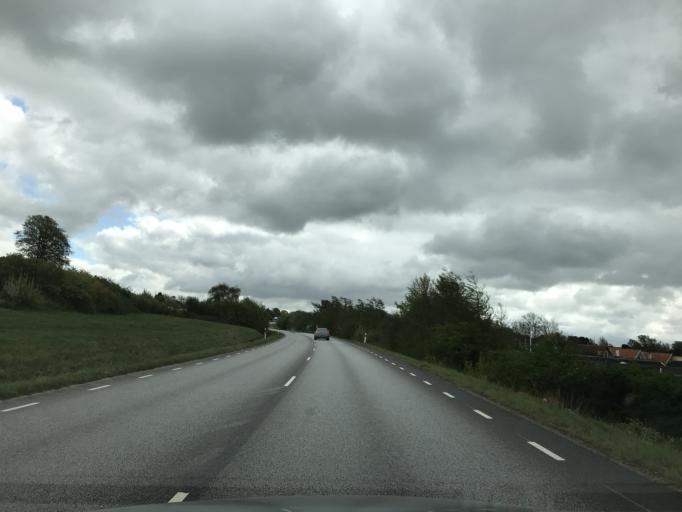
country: SE
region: Skane
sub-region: Helsingborg
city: Glumslov
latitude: 55.9449
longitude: 12.8069
